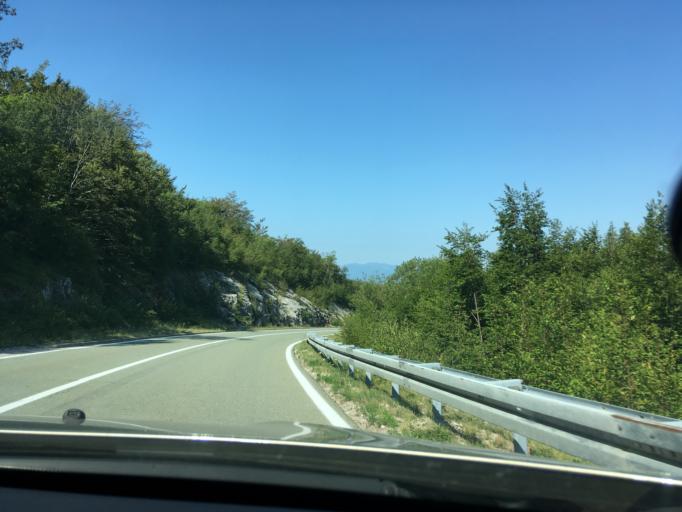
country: HR
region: Primorsko-Goranska
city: Krasica
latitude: 45.3376
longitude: 14.6029
